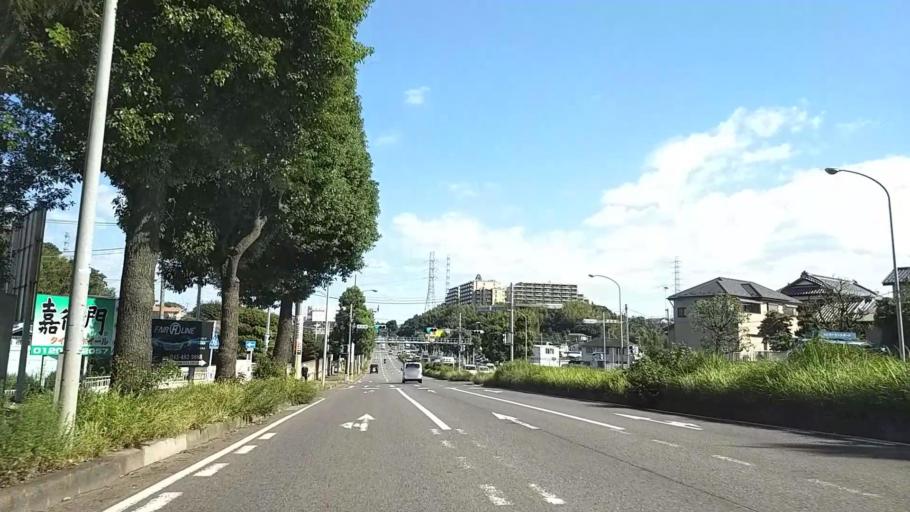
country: JP
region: Kanagawa
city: Yokohama
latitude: 35.5272
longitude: 139.5923
